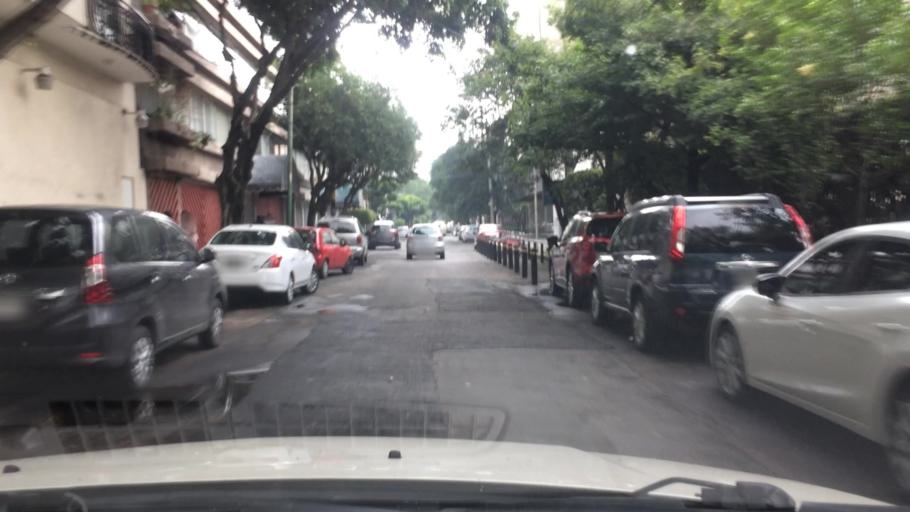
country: MX
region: Mexico City
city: Colonia del Valle
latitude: 19.3755
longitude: -99.1710
